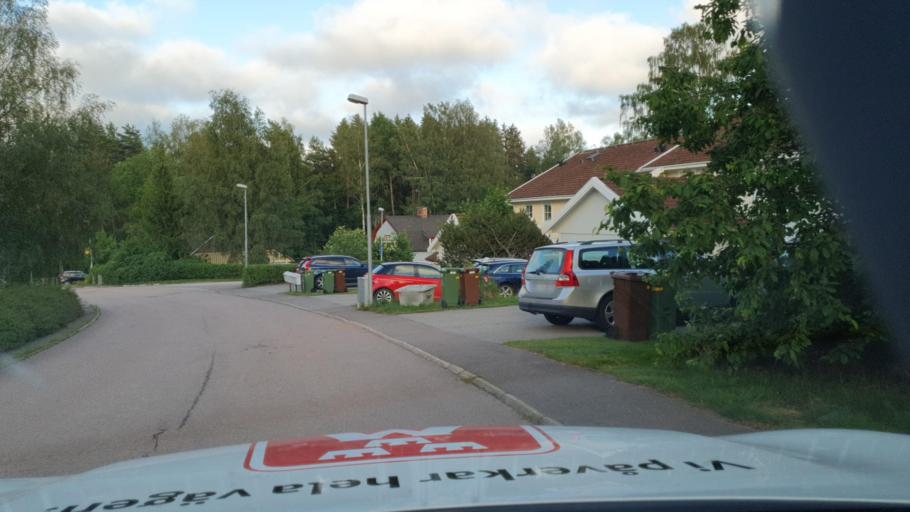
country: SE
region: Vaermland
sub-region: Kristinehamns Kommun
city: Kristinehamn
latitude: 59.3271
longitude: 14.1125
